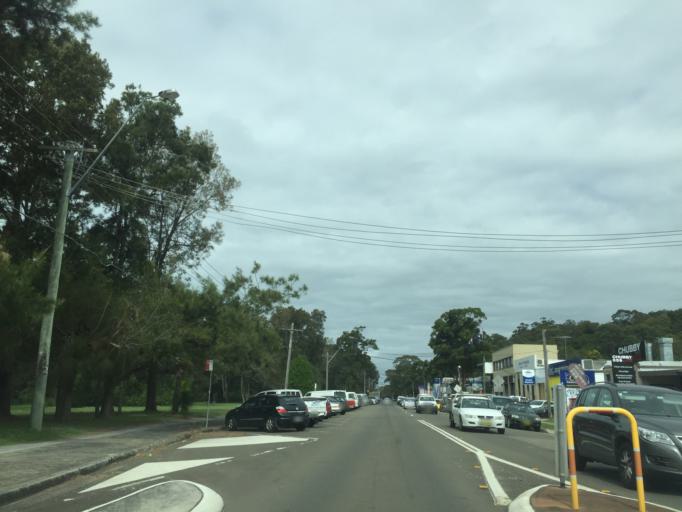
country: AU
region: New South Wales
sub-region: Pittwater
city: North Narrabeen
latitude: -33.6999
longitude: 151.2948
